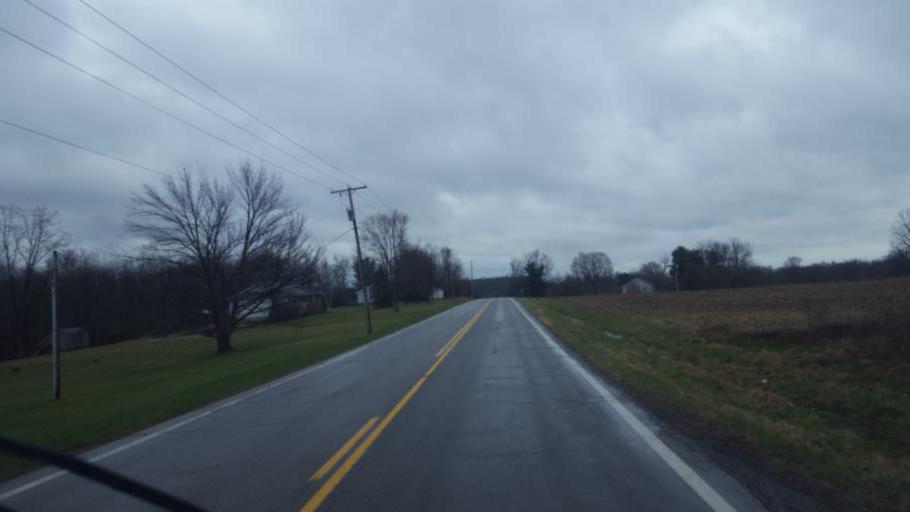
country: US
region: Ohio
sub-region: Sandusky County
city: Bellville
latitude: 40.5735
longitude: -82.5701
